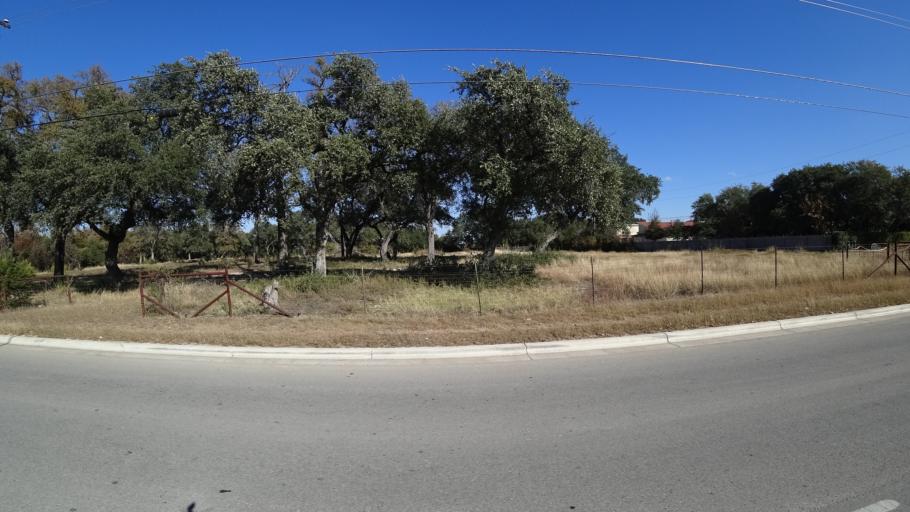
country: US
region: Texas
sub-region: Williamson County
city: Cedar Park
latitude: 30.5321
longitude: -97.8073
